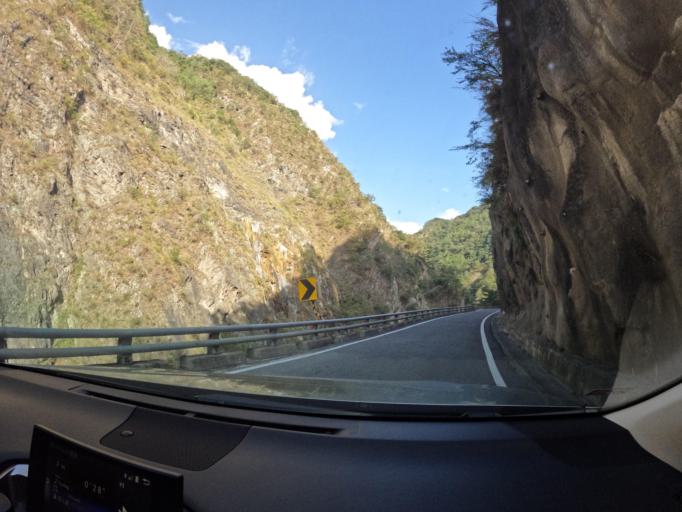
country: TW
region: Taiwan
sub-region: Taitung
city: Taitung
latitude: 23.1740
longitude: 121.0321
